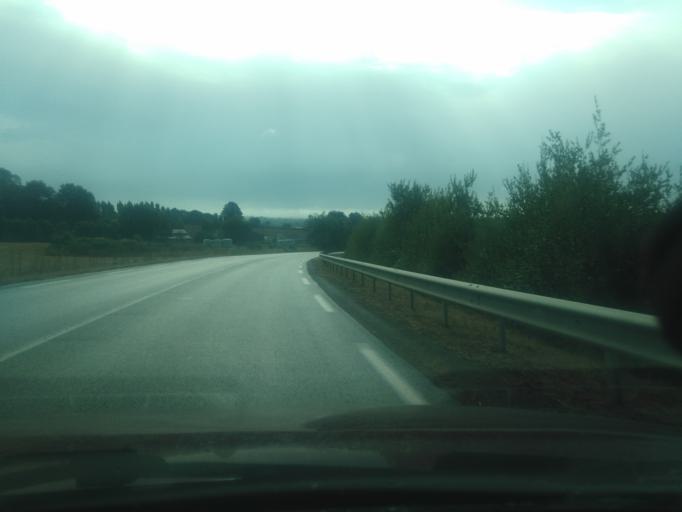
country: FR
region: Poitou-Charentes
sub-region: Departement des Deux-Sevres
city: Secondigny
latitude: 46.6185
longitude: -0.4558
